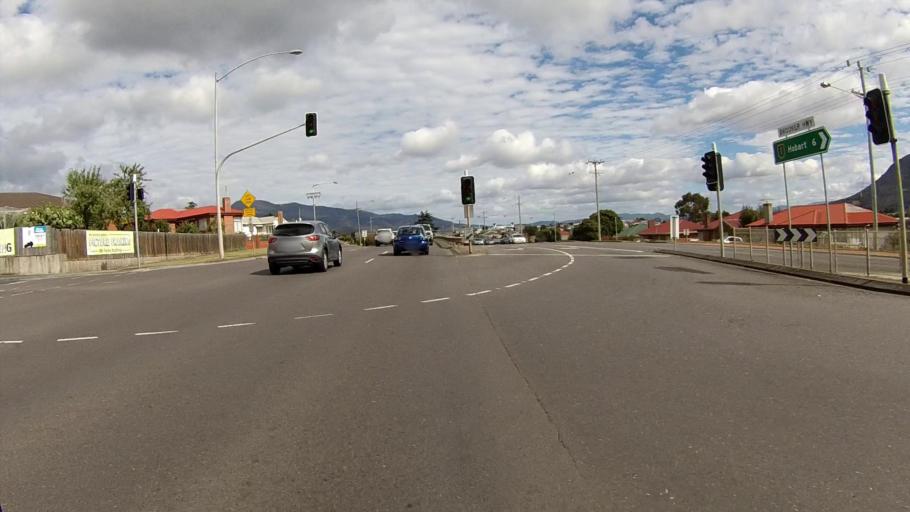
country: AU
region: Tasmania
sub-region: Glenorchy
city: Goodwood
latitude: -42.8336
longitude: 147.2980
